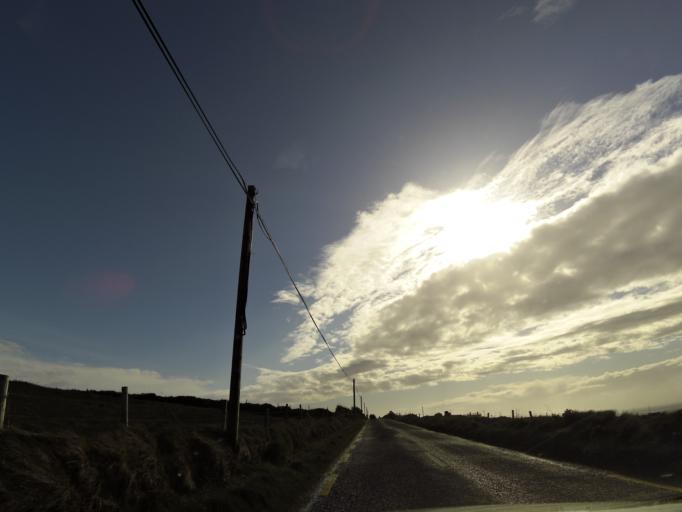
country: IE
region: Connaught
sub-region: County Galway
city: Bearna
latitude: 53.0018
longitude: -9.3770
